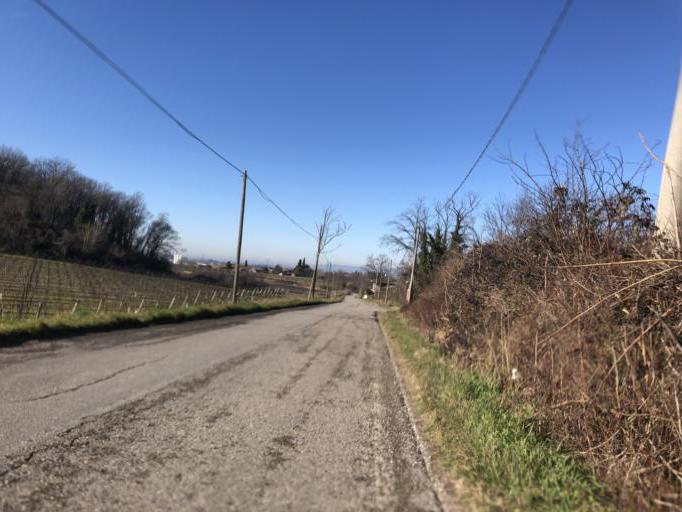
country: IT
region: Veneto
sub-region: Provincia di Verona
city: San Giorgio in Salici
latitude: 45.4259
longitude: 10.7833
